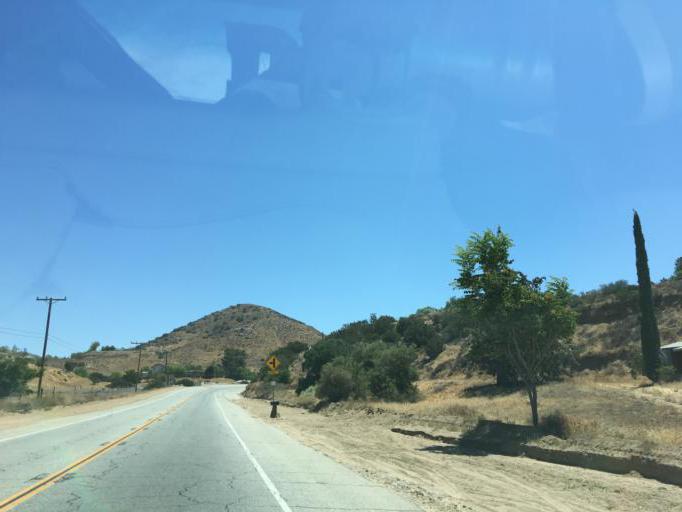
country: US
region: California
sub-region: Los Angeles County
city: Agua Dulce
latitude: 34.5199
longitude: -118.2841
